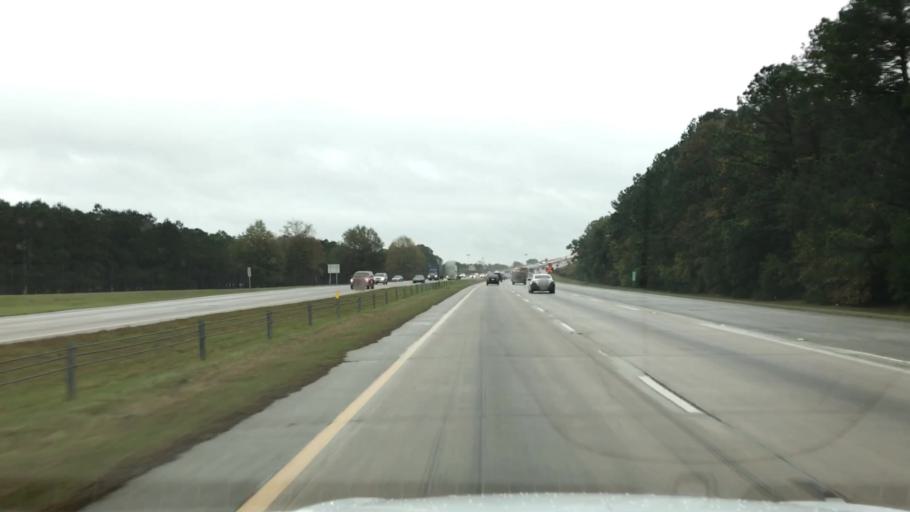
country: US
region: South Carolina
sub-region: Charleston County
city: North Charleston
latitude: 32.8681
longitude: -79.9102
